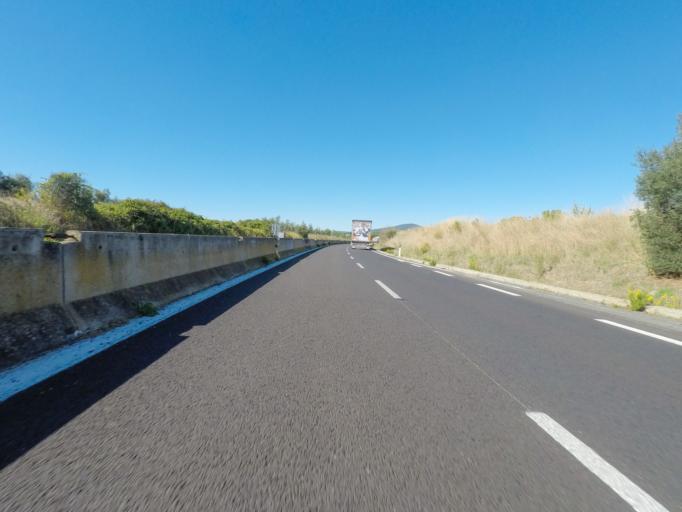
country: IT
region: Latium
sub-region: Provincia di Viterbo
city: Pescia Romana
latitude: 42.4087
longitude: 11.4791
